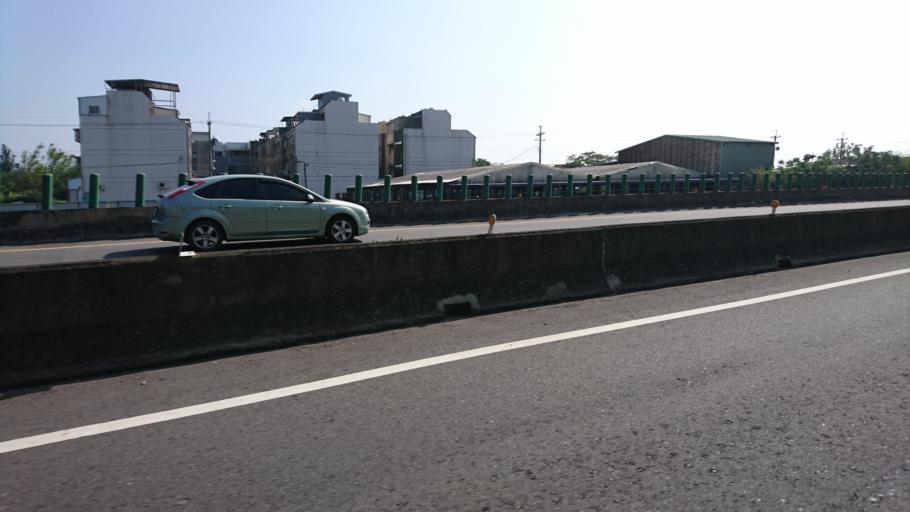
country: TW
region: Taiwan
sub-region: Miaoli
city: Miaoli
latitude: 24.6893
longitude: 120.8548
